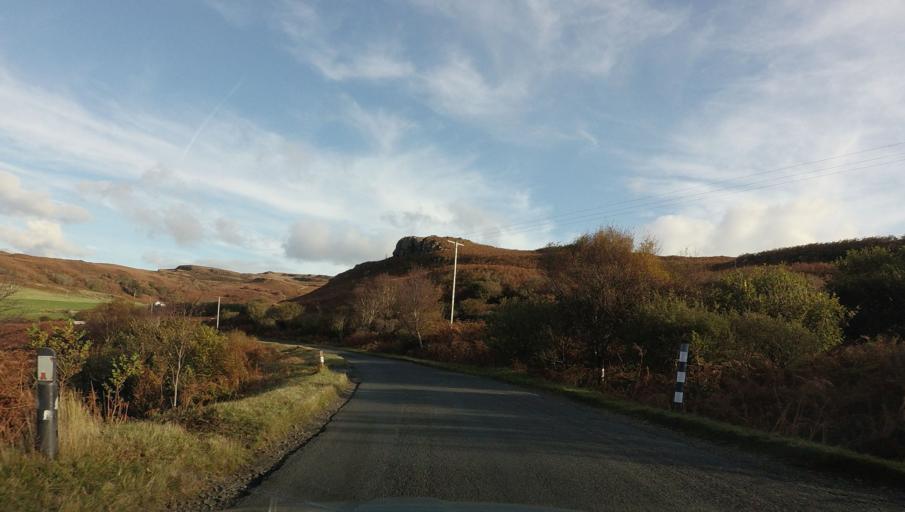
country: GB
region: Scotland
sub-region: Argyll and Bute
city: Isle Of Mull
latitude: 56.3359
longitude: -6.1440
